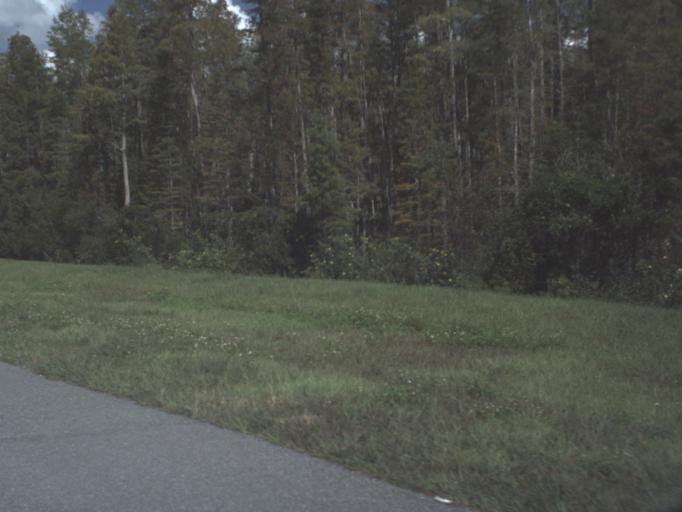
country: US
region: Florida
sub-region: Pasco County
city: Shady Hills
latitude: 28.2999
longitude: -82.5502
